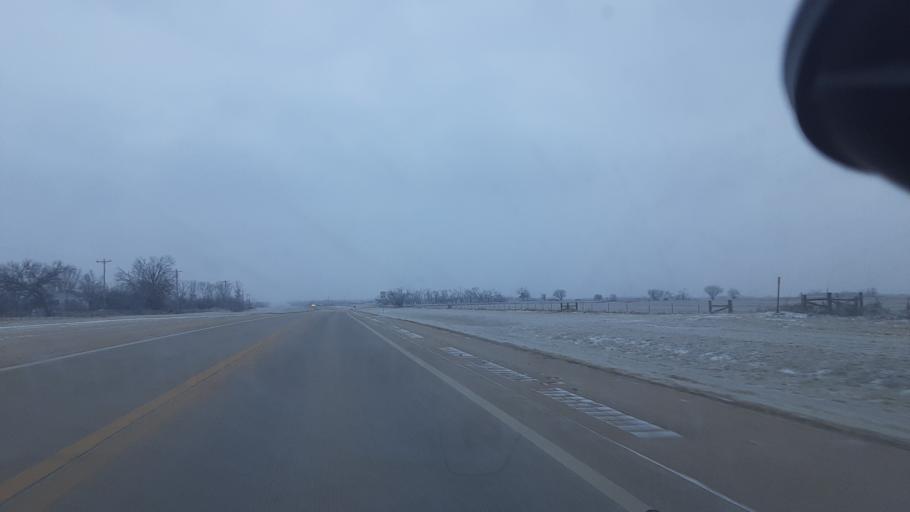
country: US
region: Oklahoma
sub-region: Payne County
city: Perkins
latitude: 35.9854
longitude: -97.0957
